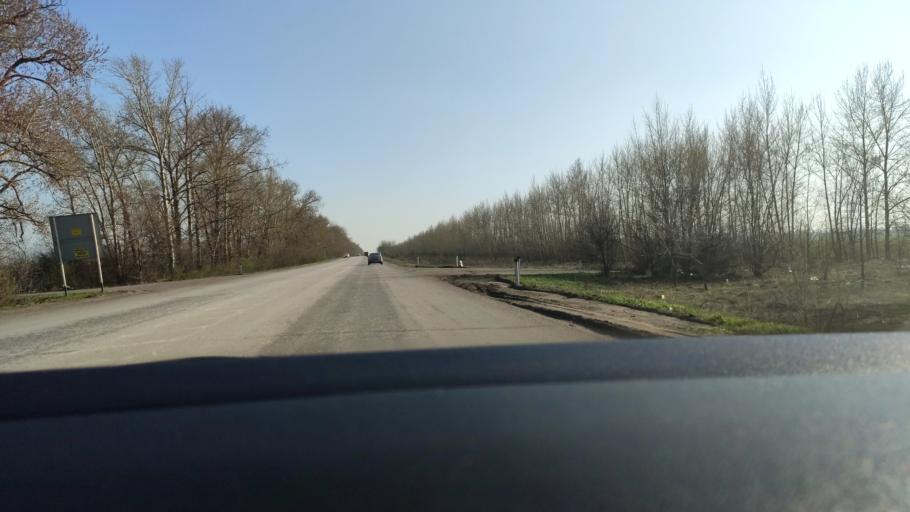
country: RU
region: Voronezj
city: Maslovka
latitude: 51.4662
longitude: 39.3052
